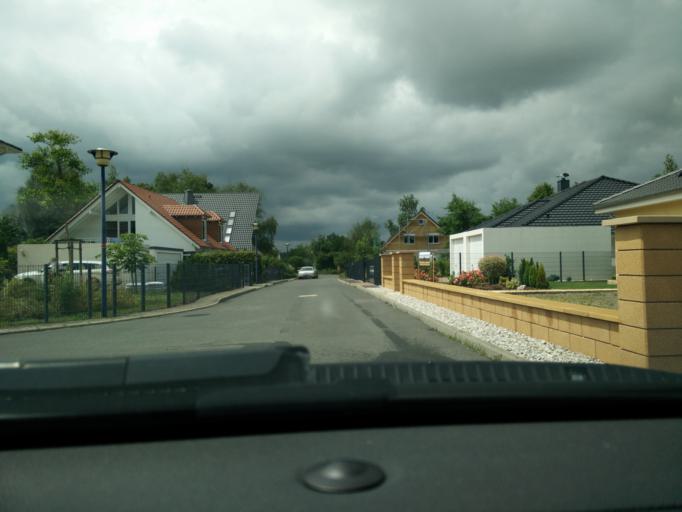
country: DE
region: Saxony
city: Bad Lausick
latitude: 51.1479
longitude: 12.6427
